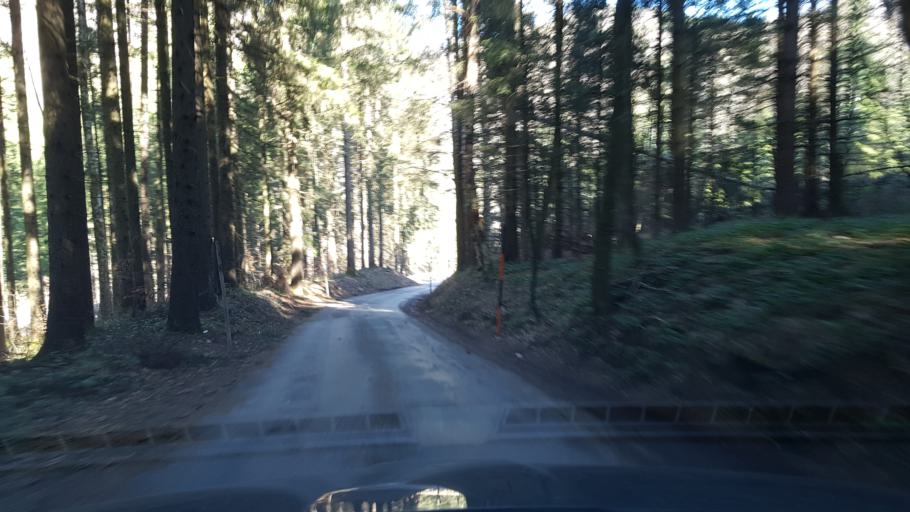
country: AT
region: Salzburg
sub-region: Politischer Bezirk Salzburg-Umgebung
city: Ebenau
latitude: 47.8077
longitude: 13.1931
